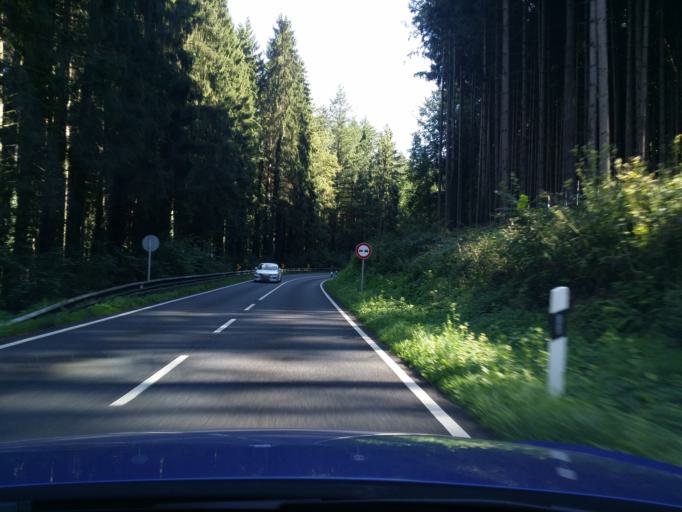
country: LU
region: Luxembourg
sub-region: Canton de Capellen
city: Kopstal
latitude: 49.6977
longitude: 6.0882
